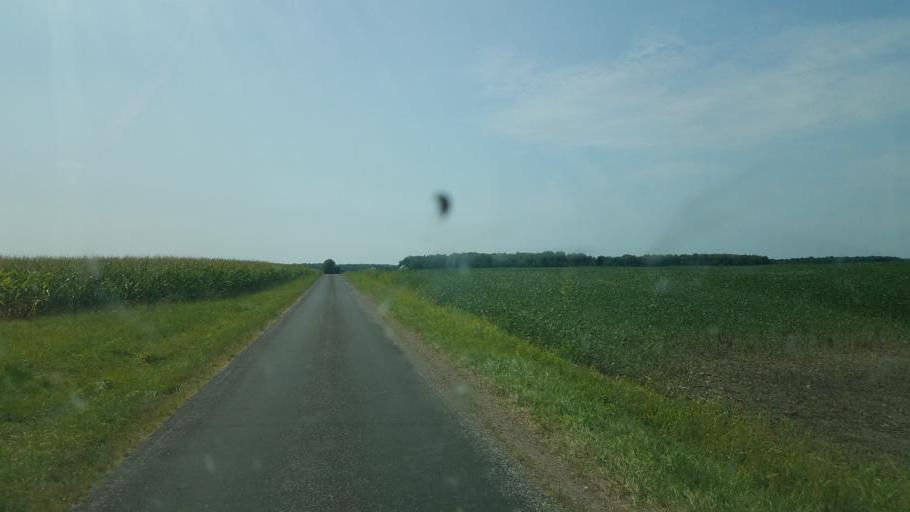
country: US
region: Ohio
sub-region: Delaware County
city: Ashley
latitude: 40.5027
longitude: -83.0196
